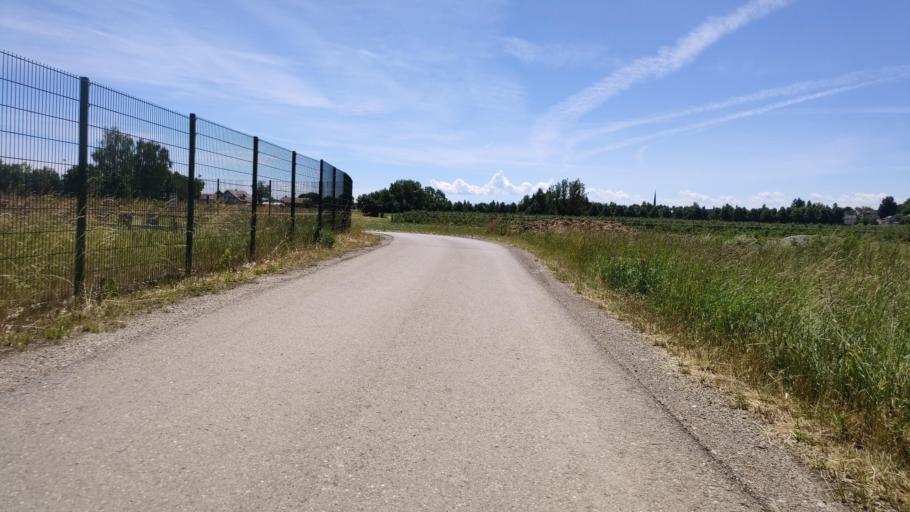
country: DE
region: Bavaria
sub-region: Swabia
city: Bad Worishofen
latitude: 48.0190
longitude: 10.5915
